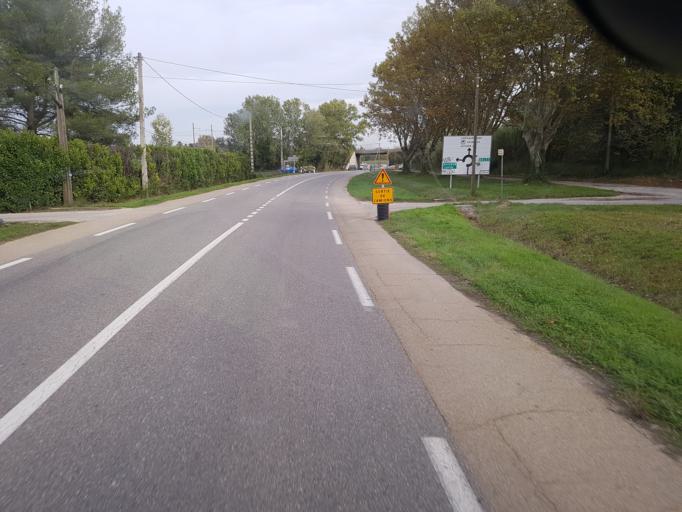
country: FR
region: Provence-Alpes-Cote d'Azur
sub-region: Departement des Bouches-du-Rhone
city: Rognonas
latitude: 43.9089
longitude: 4.7876
